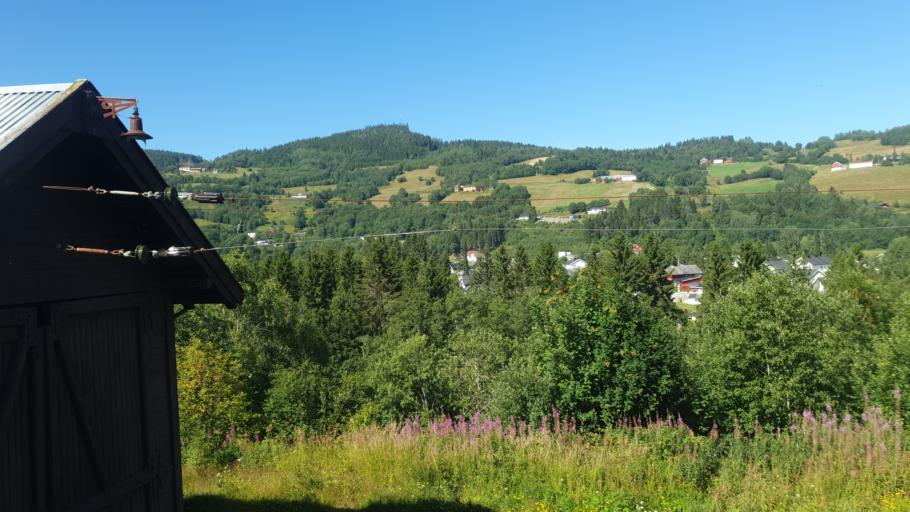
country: NO
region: Sor-Trondelag
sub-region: Meldal
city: Meldal
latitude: 63.1679
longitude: 9.7462
